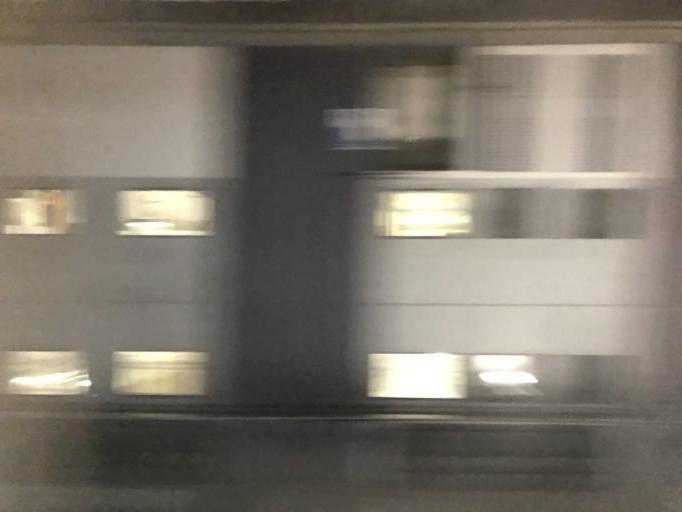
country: HK
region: Sha Tin
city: Sha Tin
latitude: 22.4025
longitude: 114.2033
